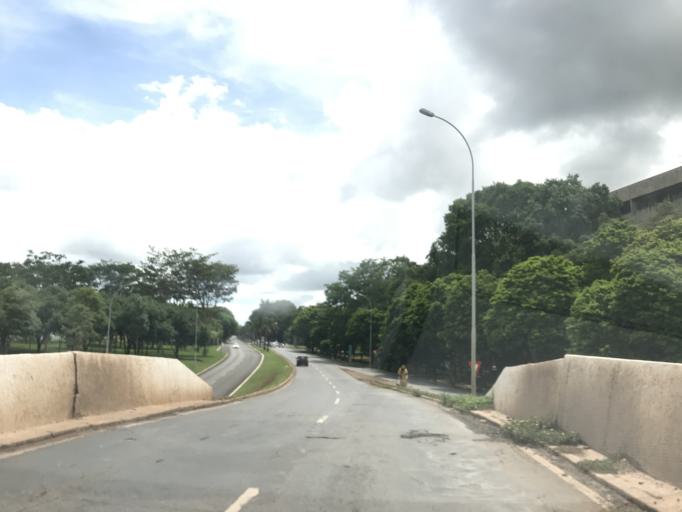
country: BR
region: Federal District
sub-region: Brasilia
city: Brasilia
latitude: -15.8347
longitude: -47.9243
